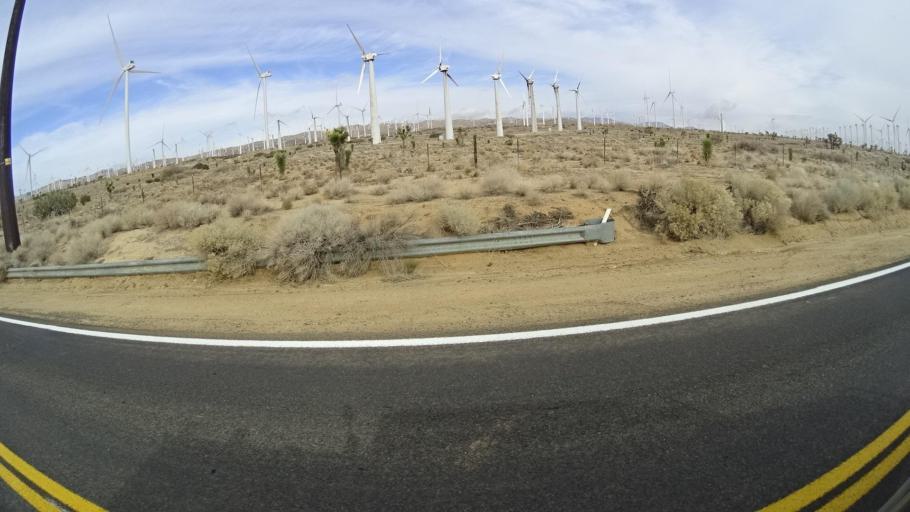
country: US
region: California
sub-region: Kern County
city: Mojave
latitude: 35.0384
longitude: -118.2961
